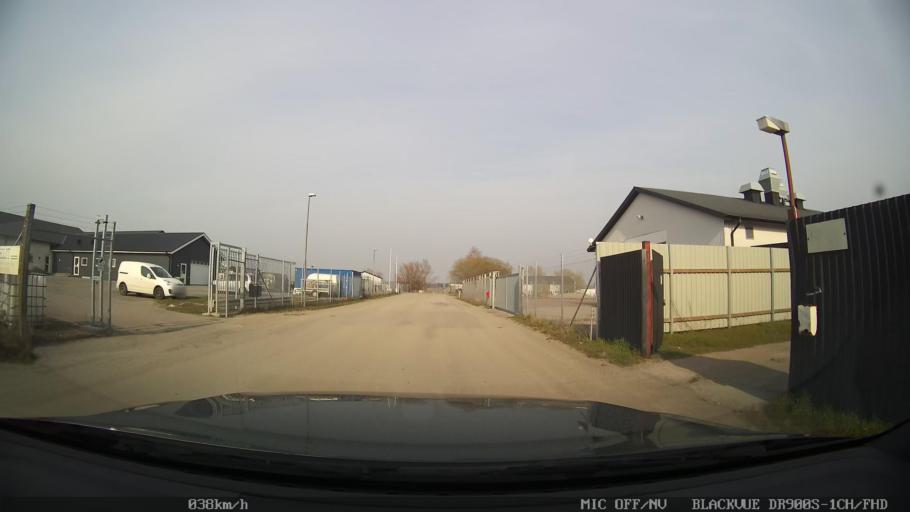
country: SE
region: Skane
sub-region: Ystads Kommun
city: Ystad
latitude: 55.4454
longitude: 13.8518
